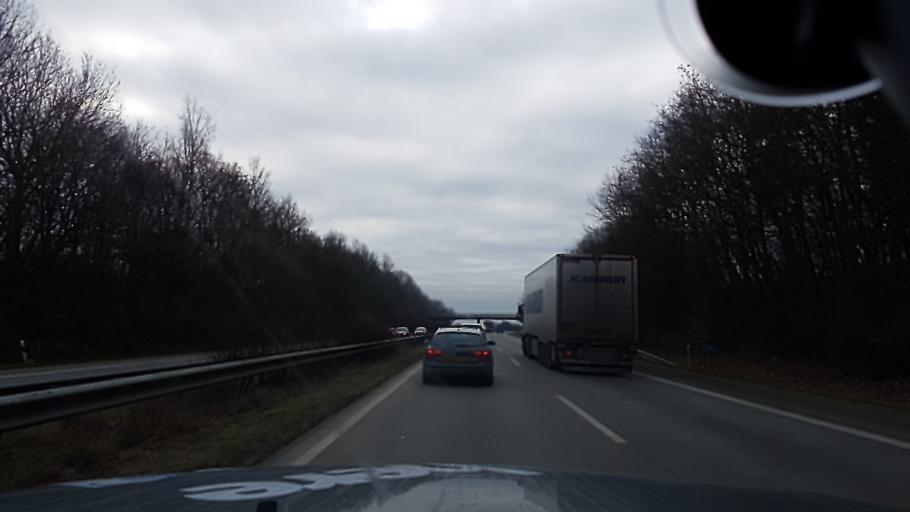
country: DE
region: Schleswig-Holstein
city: Ratekau
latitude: 53.9911
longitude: 10.7334
